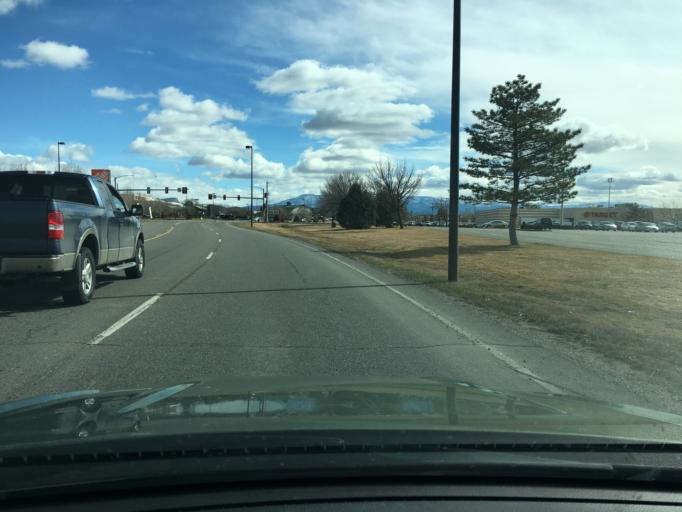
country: US
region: Colorado
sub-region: Mesa County
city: Redlands
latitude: 39.0946
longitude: -108.6042
